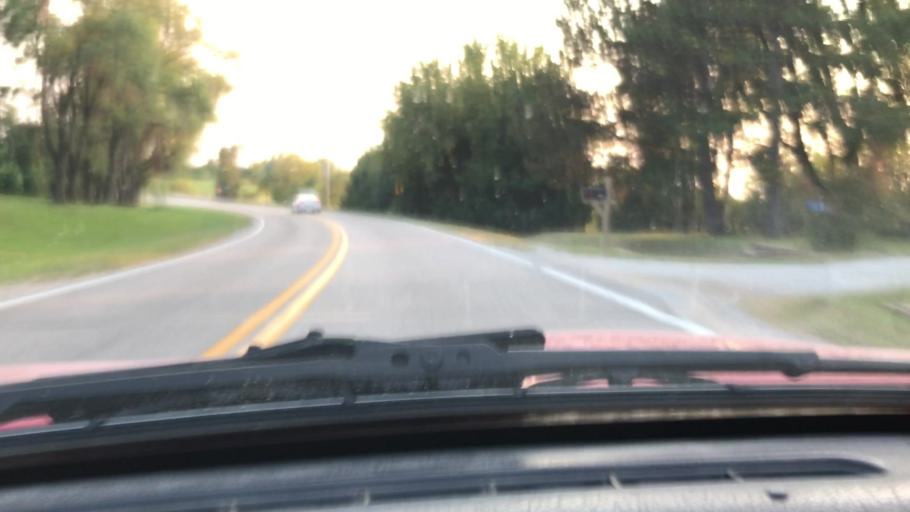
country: US
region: Nebraska
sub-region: Lancaster County
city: Lincoln
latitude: 40.7678
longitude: -96.7390
